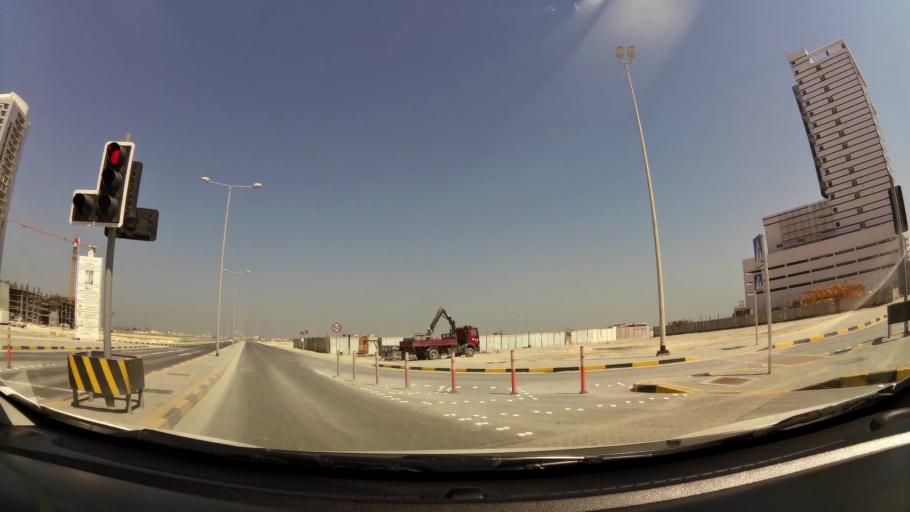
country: BH
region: Manama
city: Manama
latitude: 26.2211
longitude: 50.6125
